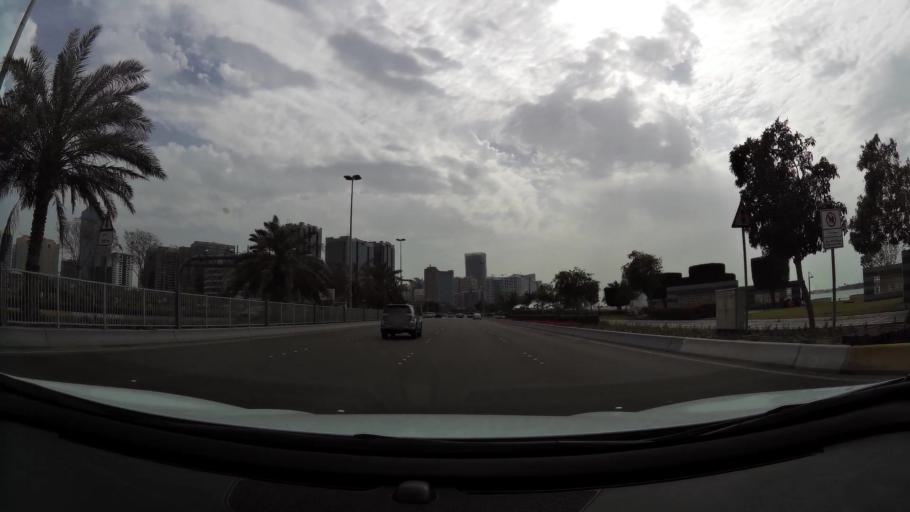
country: AE
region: Abu Dhabi
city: Abu Dhabi
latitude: 24.4799
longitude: 54.3461
